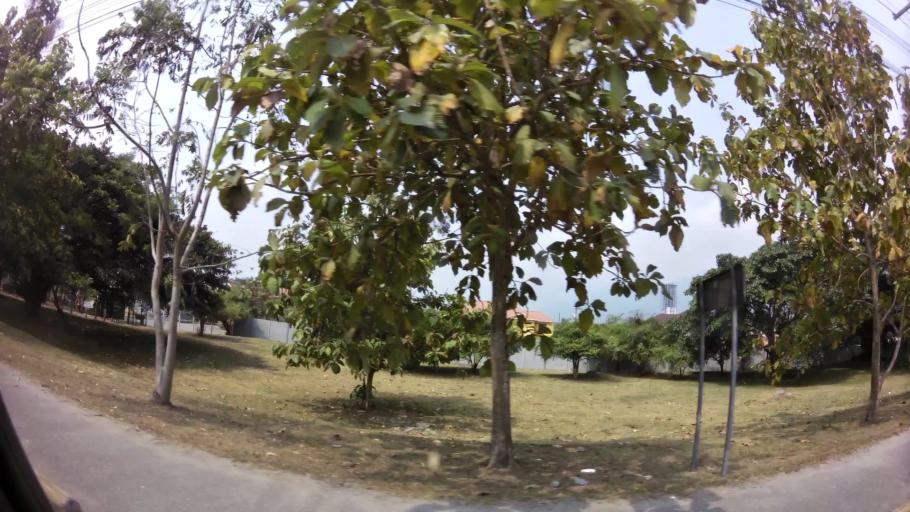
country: HN
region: Cortes
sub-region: San Pedro Sula
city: Pena Blanca
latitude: 15.5553
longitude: -88.0141
